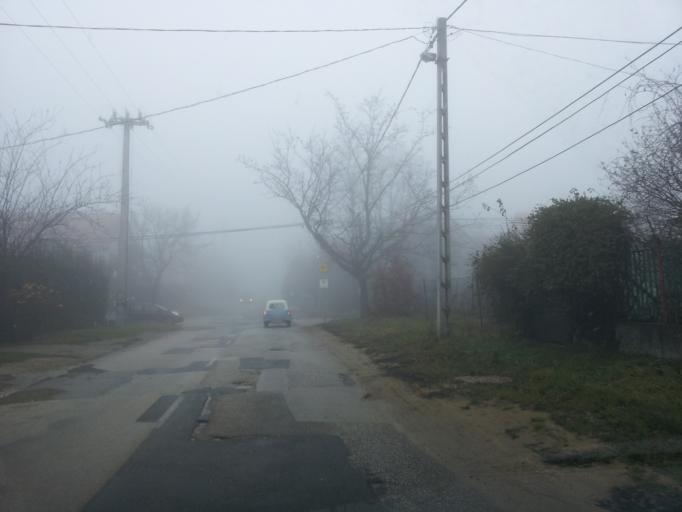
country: HU
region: Pest
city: Toeroekbalint
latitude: 47.4226
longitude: 18.8812
